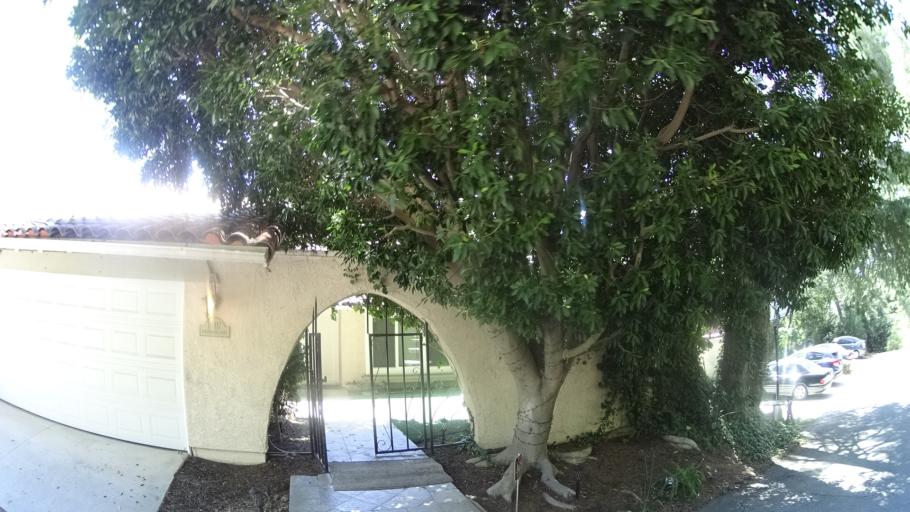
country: US
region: California
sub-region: Los Angeles County
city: Sherman Oaks
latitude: 34.1185
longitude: -118.4469
